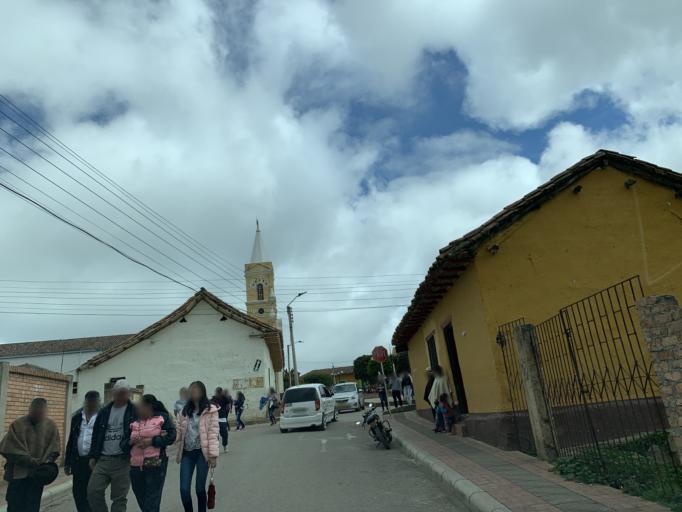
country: CO
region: Boyaca
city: Tunja
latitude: 5.5771
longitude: -73.3673
